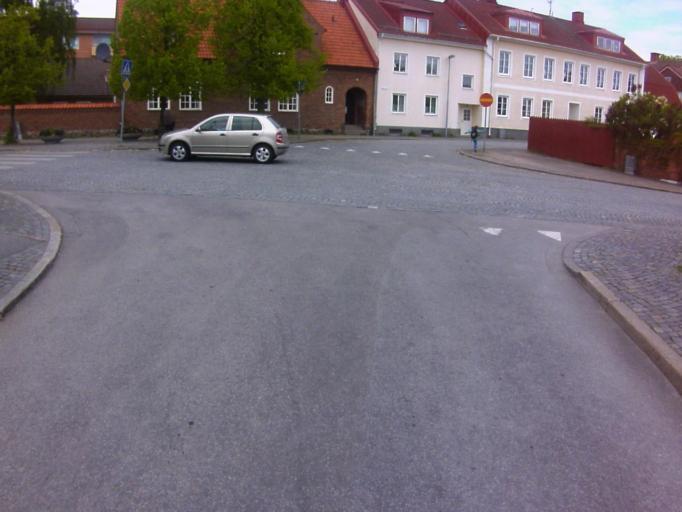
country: SE
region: Blekinge
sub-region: Solvesborgs Kommun
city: Soelvesborg
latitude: 56.0524
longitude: 14.5816
